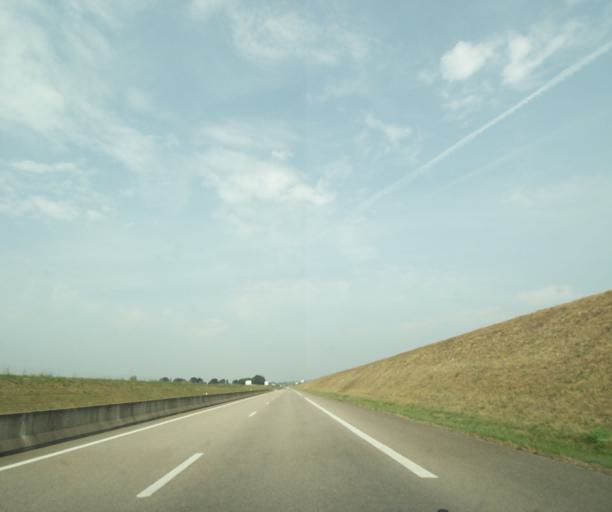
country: FR
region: Lower Normandy
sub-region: Departement du Calvados
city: Falaise
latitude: 48.8668
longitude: -0.2017
